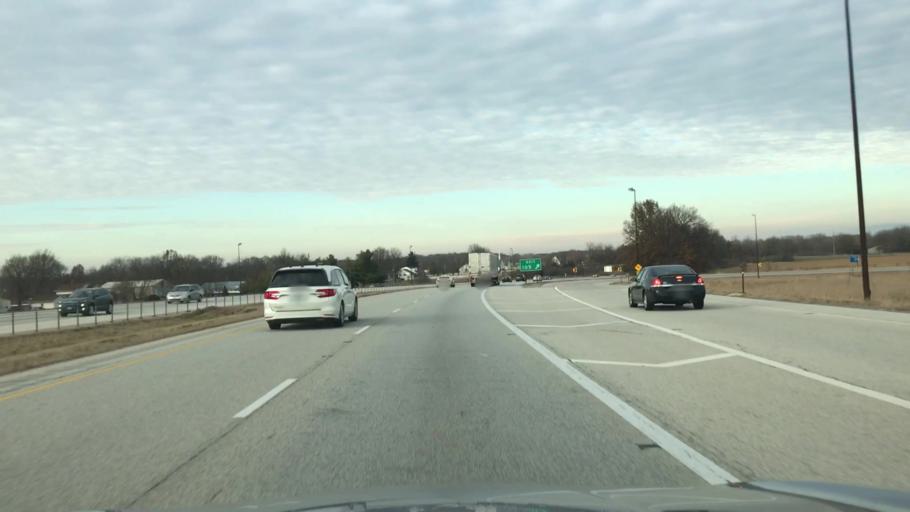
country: US
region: Illinois
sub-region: Sangamon County
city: Sherman
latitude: 39.9053
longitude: -89.5952
